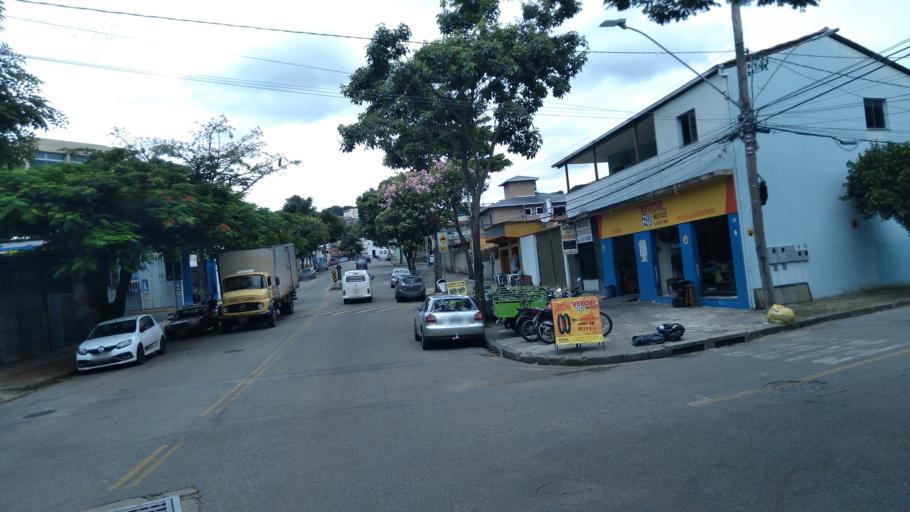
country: BR
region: Minas Gerais
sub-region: Contagem
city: Contagem
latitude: -19.9152
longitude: -44.0013
